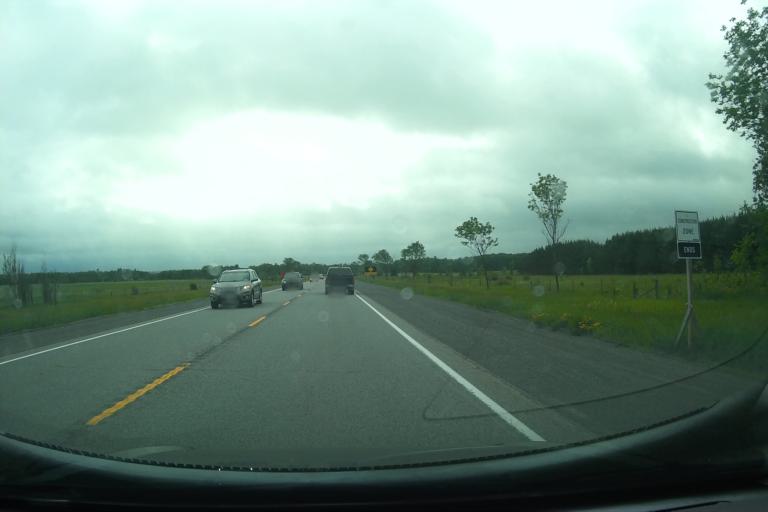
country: CA
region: Ontario
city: Arnprior
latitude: 45.4410
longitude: -76.4860
